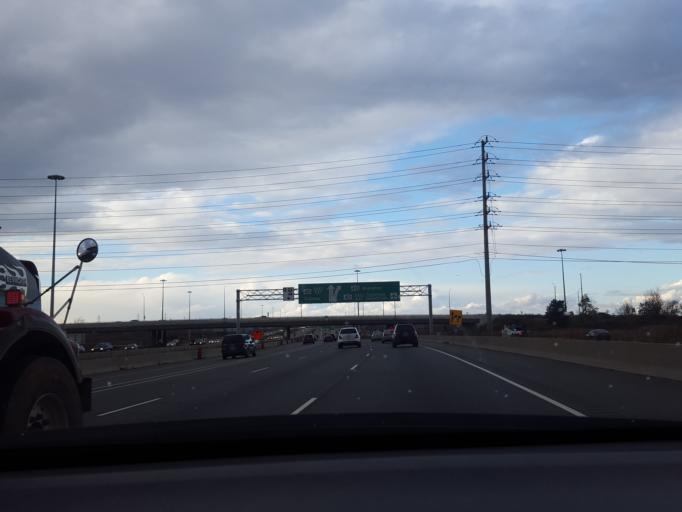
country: CA
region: Ontario
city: Mississauga
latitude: 43.6202
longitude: -79.6344
